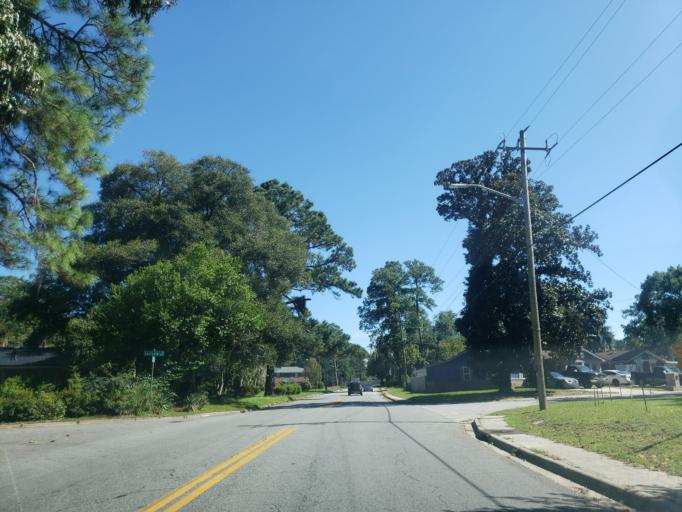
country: US
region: Georgia
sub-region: Chatham County
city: Thunderbolt
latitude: 32.0359
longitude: -81.0734
